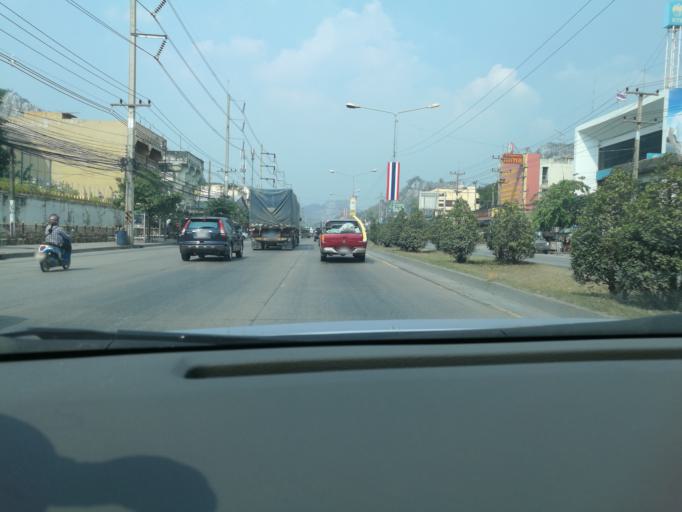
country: TH
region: Sara Buri
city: Phra Phutthabat
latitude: 14.6890
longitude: 100.8703
